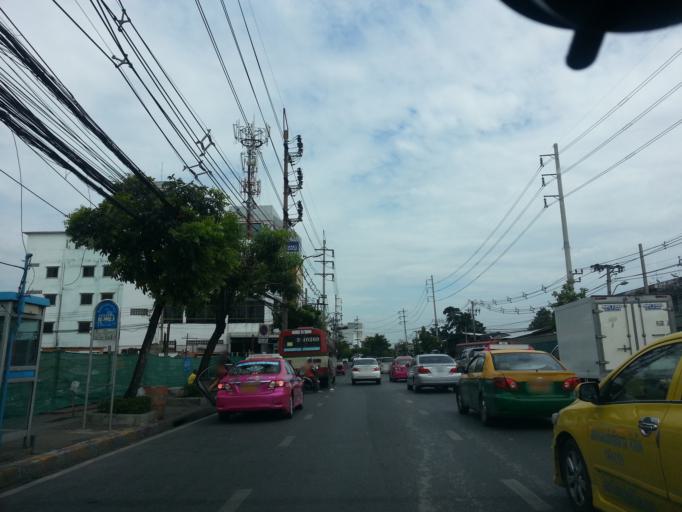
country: TH
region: Bangkok
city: Khlong Toei
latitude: 13.7196
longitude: 100.5606
